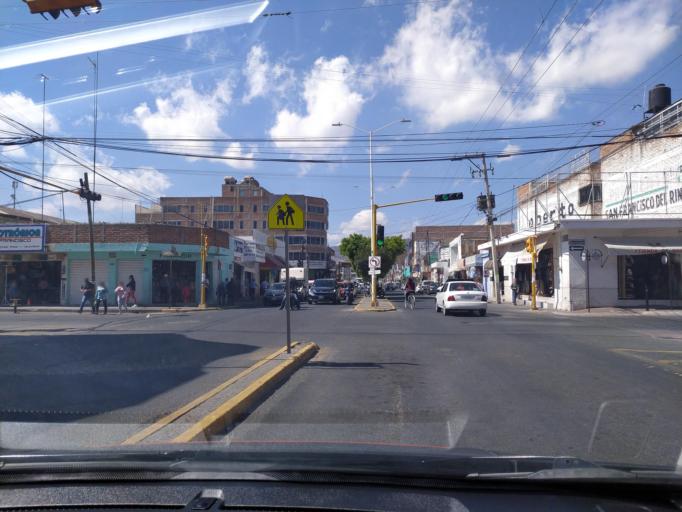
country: LA
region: Oudomxai
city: Muang La
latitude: 21.0158
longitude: 101.8567
